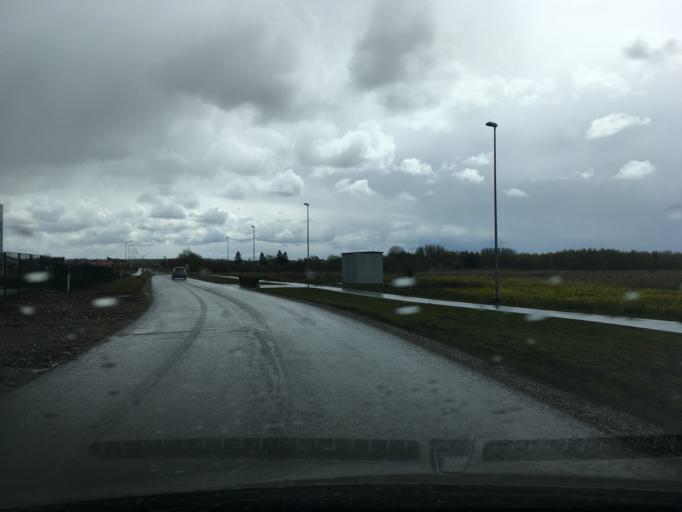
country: EE
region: Harju
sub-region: Joelaehtme vald
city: Loo
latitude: 59.4468
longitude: 24.9566
